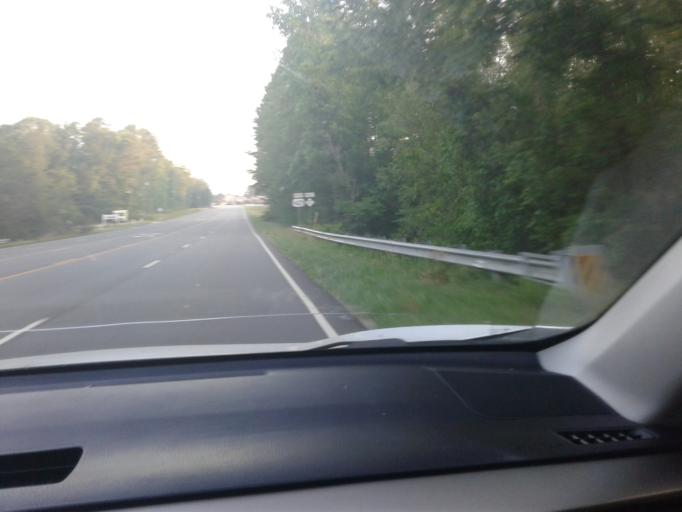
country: US
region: North Carolina
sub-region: Harnett County
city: Buies Creek
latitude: 35.3998
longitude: -78.7345
